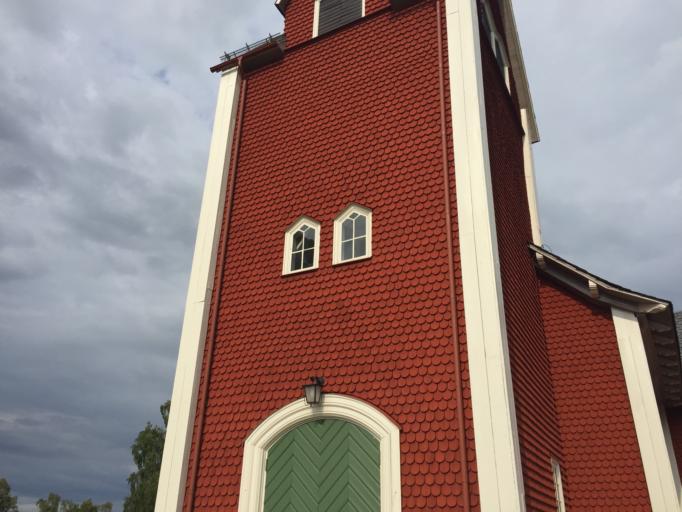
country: SE
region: Vaermland
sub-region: Filipstads Kommun
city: Lesjofors
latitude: 60.0312
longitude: 14.1286
